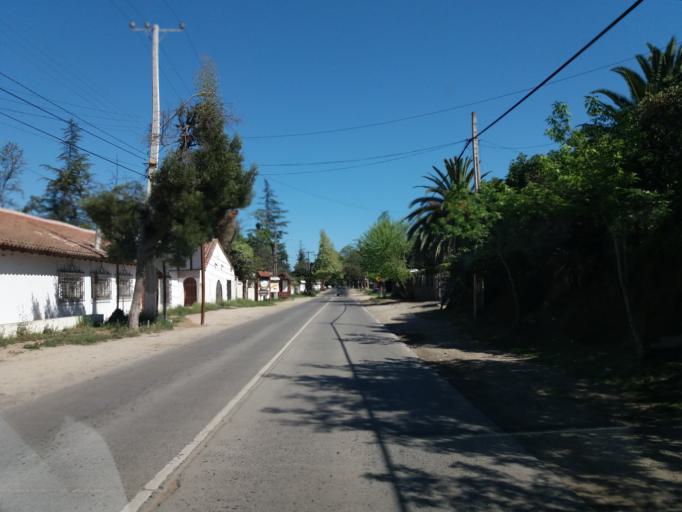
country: CL
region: Valparaiso
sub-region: Provincia de Marga Marga
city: Limache
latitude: -33.0002
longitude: -71.2112
